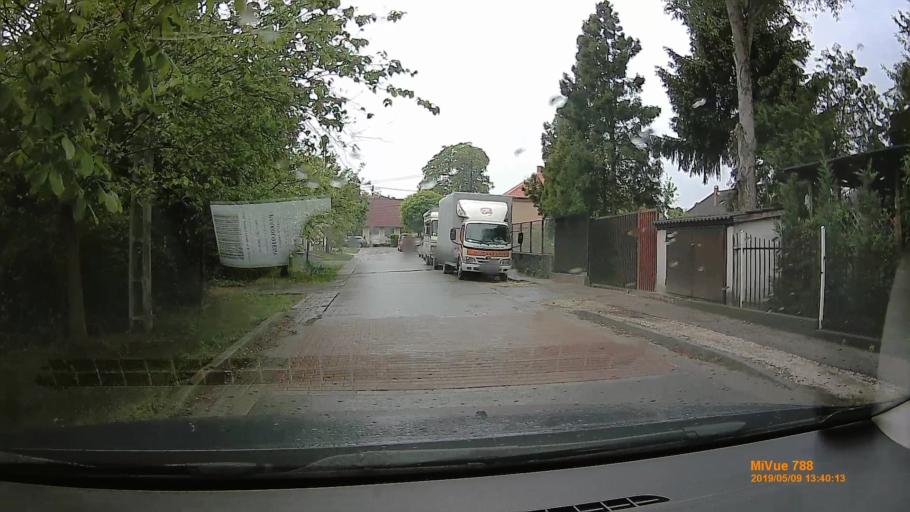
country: HU
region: Budapest
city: Budapest XVI. keruelet
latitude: 47.5318
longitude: 19.1973
